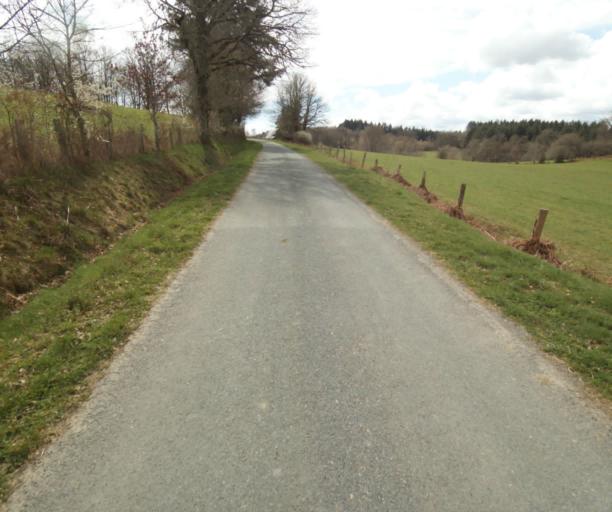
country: FR
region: Limousin
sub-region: Departement de la Correze
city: Correze
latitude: 45.3832
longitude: 1.9619
